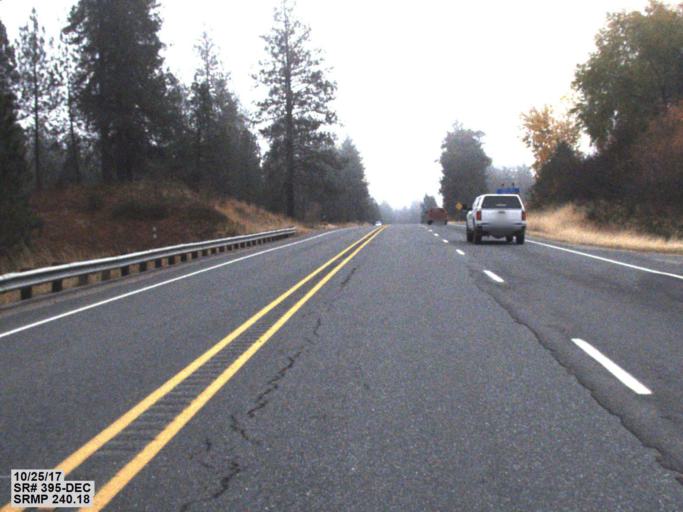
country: US
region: Washington
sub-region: Stevens County
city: Kettle Falls
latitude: 48.6121
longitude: -118.0951
